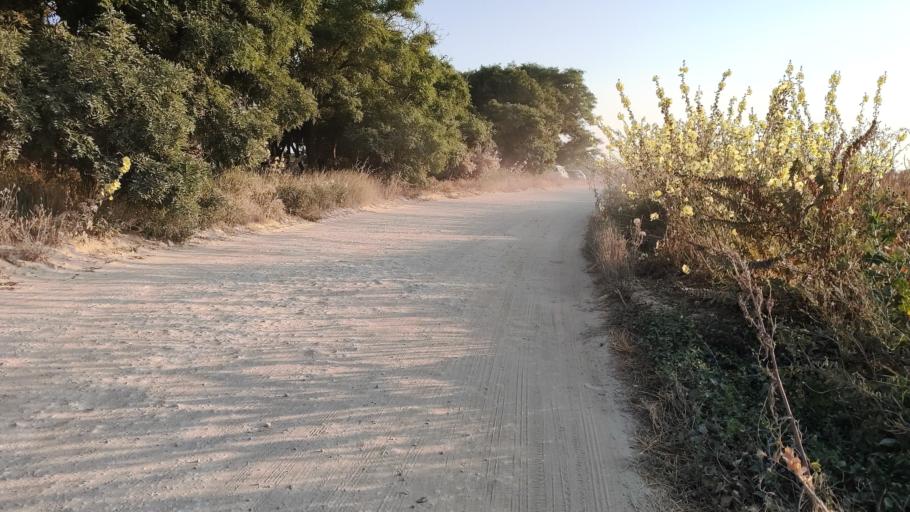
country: RU
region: Krasnodarskiy
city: Blagovetschenskaya
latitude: 45.0666
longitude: 37.0530
